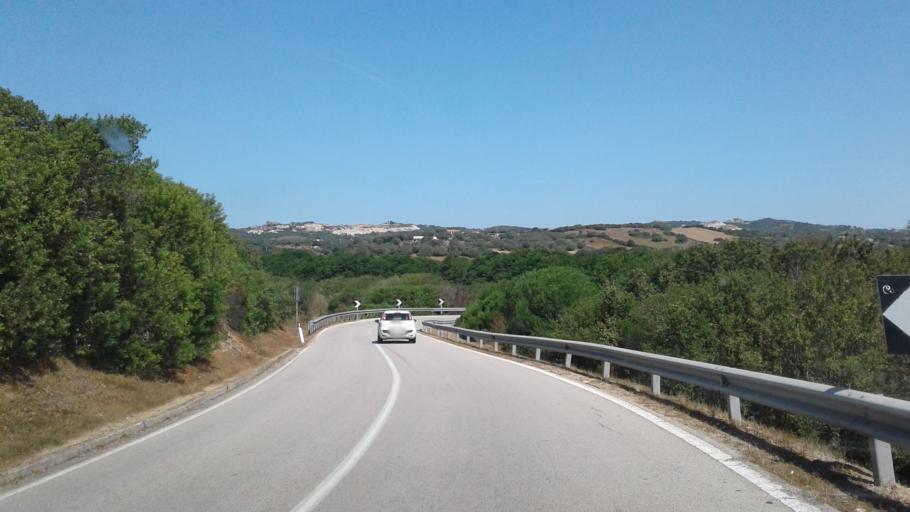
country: IT
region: Sardinia
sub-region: Provincia di Olbia-Tempio
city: Luogosanto
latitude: 41.1145
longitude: 9.2628
